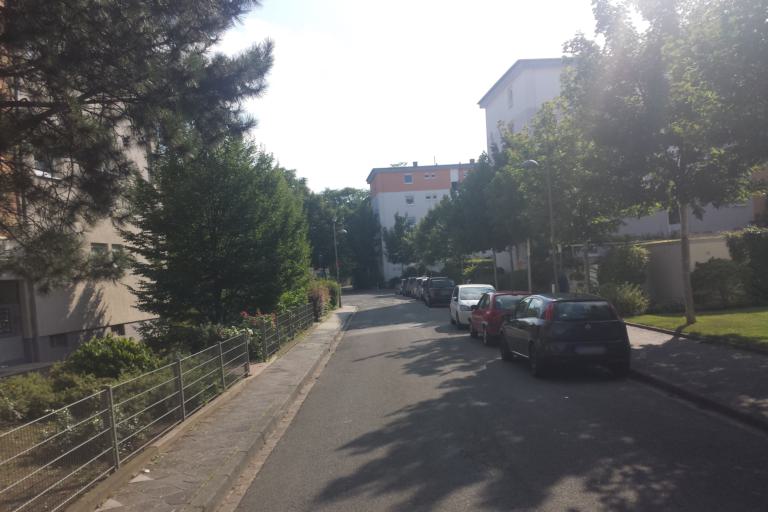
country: DE
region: Baden-Wuerttemberg
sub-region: Karlsruhe Region
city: Mannheim
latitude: 49.5229
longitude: 8.4985
